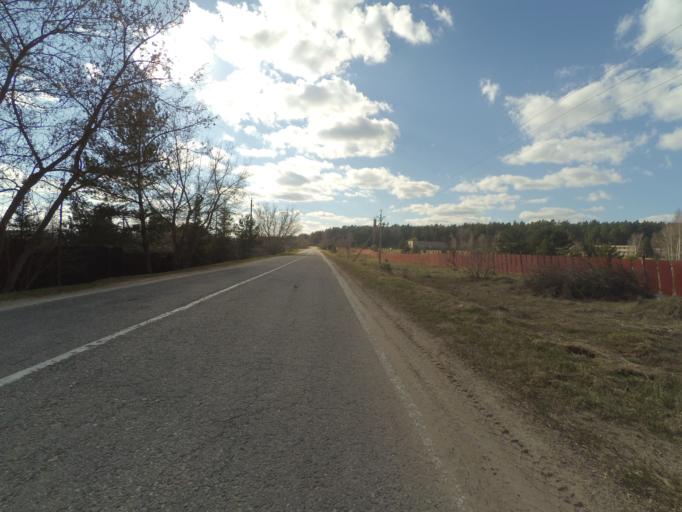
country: RU
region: Moskovskaya
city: Stupino
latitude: 54.8527
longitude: 37.8831
